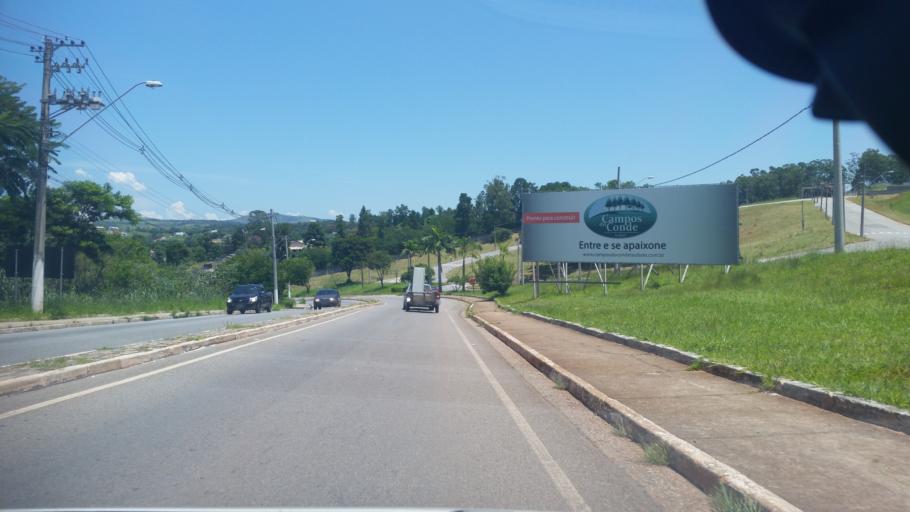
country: BR
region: Sao Paulo
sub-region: Taubate
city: Taubate
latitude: -23.0632
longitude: -45.5562
